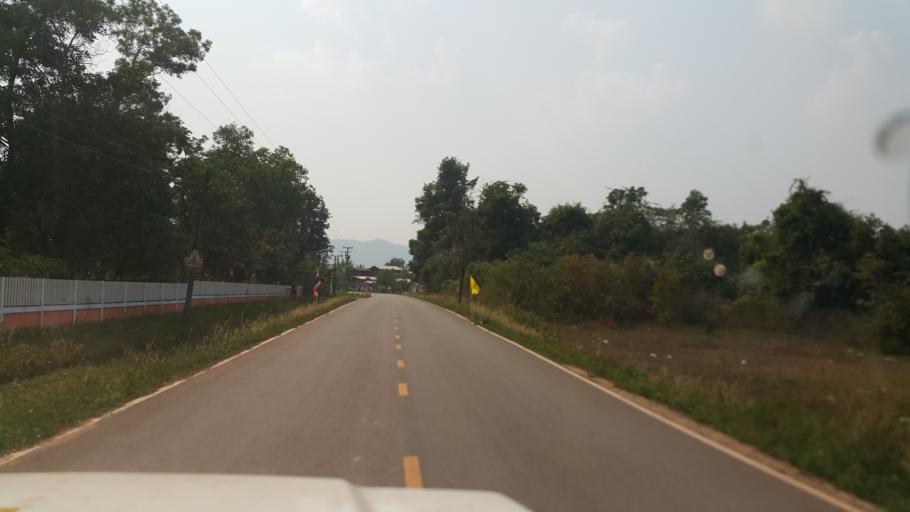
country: TH
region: Nakhon Phanom
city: Ban Phaeng
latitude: 17.9594
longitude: 104.1814
